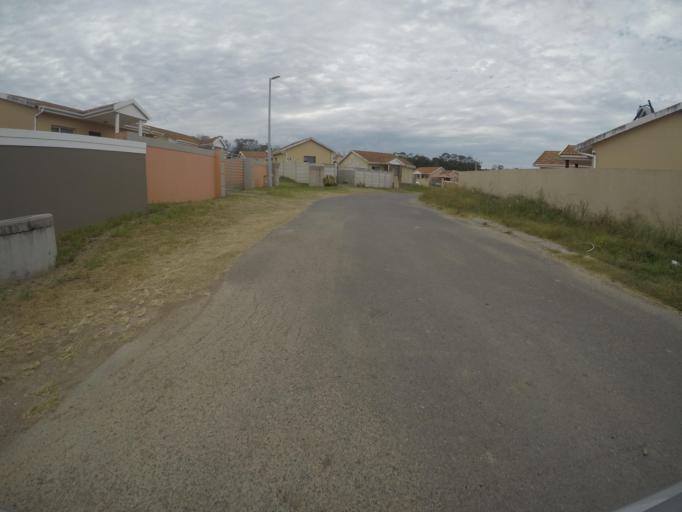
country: ZA
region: Eastern Cape
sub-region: Buffalo City Metropolitan Municipality
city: East London
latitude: -32.9913
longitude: 27.8433
